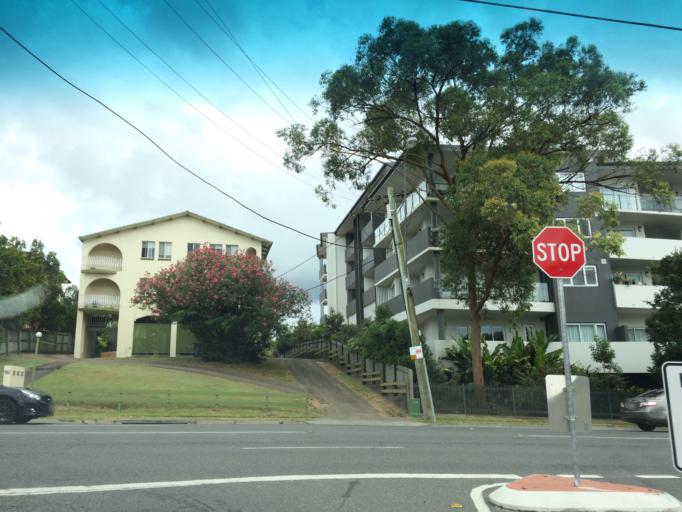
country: AU
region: Queensland
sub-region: Brisbane
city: Toowong
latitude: -27.4945
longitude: 153.0028
